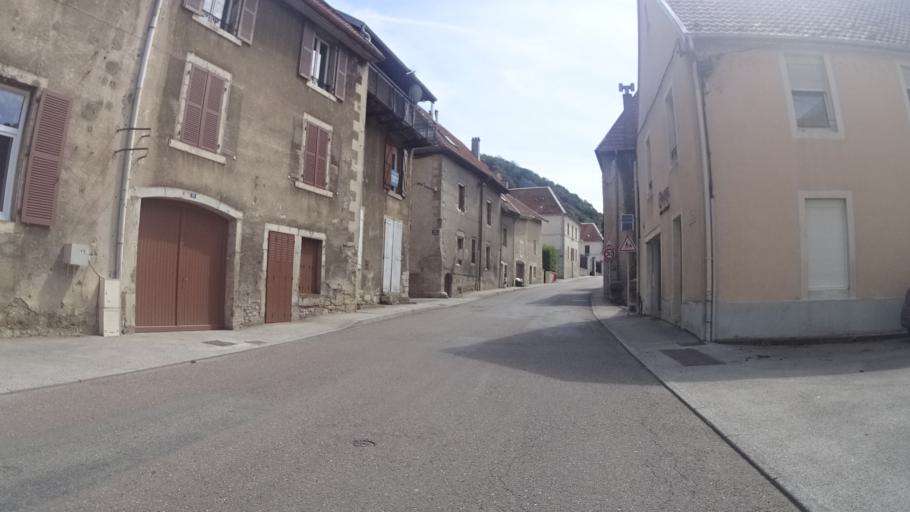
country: FR
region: Franche-Comte
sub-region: Departement du Doubs
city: Clerval
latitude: 47.3924
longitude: 6.4978
